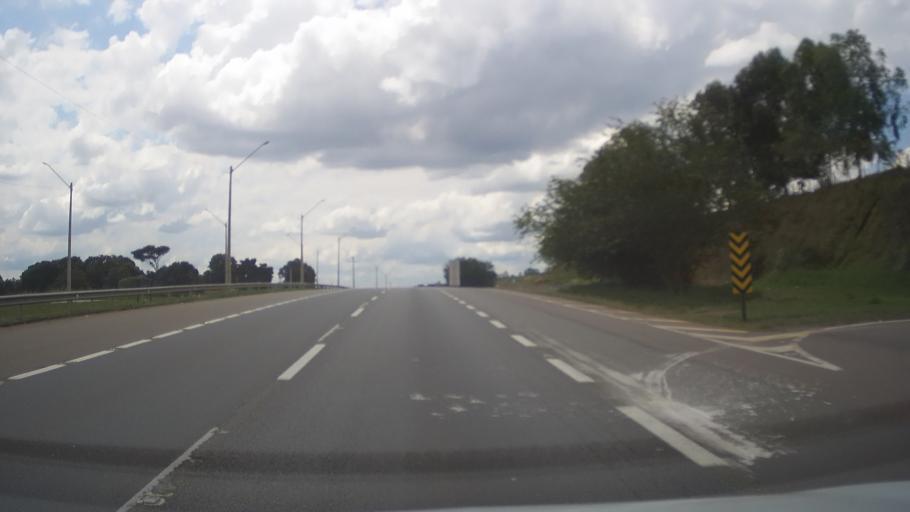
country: BR
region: Minas Gerais
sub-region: Nepomuceno
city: Nepomuceno
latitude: -21.2657
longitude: -45.1381
